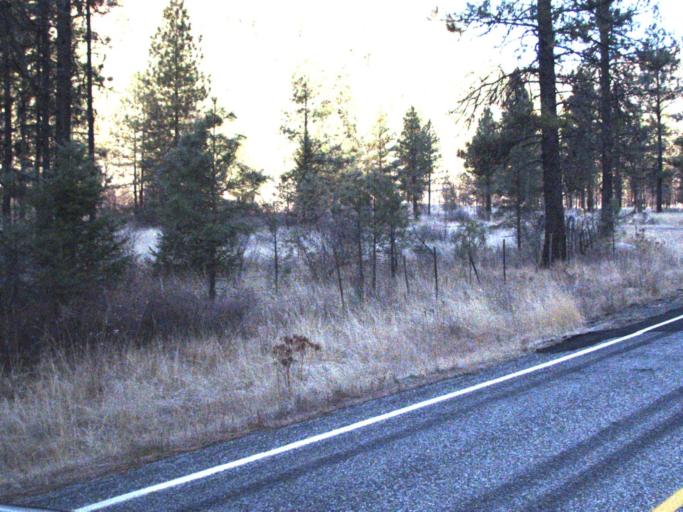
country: US
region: Washington
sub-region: Ferry County
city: Republic
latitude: 48.4014
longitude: -118.7318
